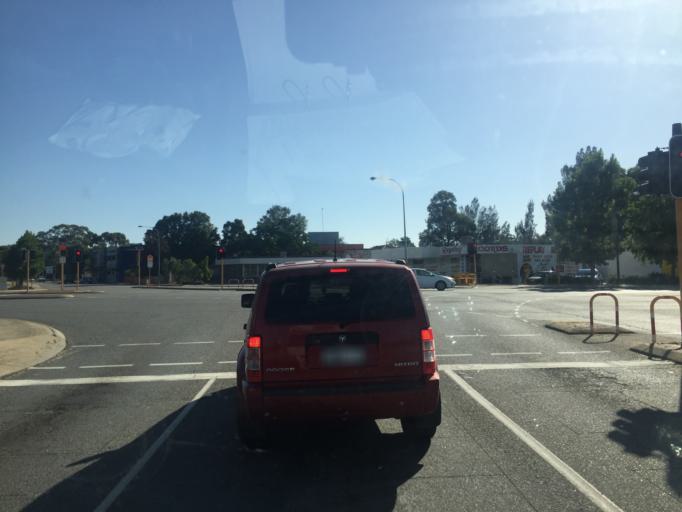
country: AU
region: Western Australia
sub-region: Gosnells
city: Kenwick
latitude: -32.0364
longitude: 115.9688
